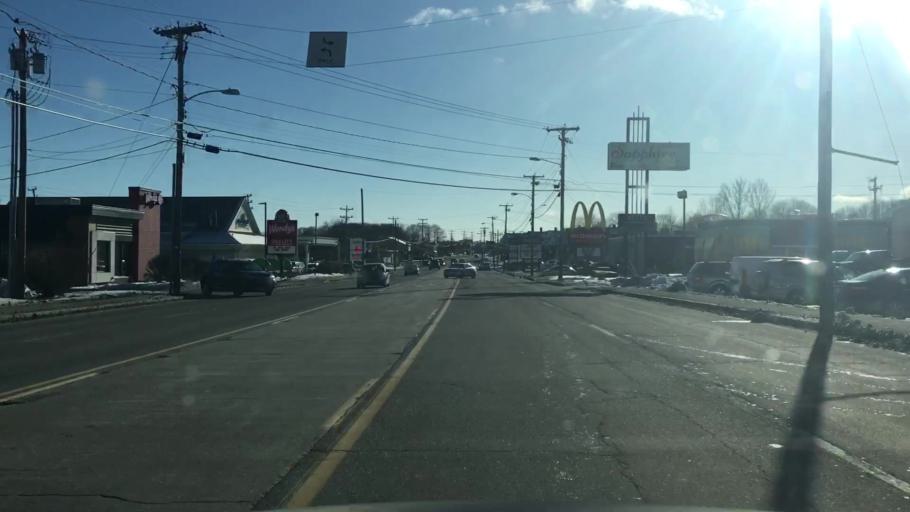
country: US
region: Maine
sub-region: Androscoggin County
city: Auburn
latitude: 44.1078
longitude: -70.2259
